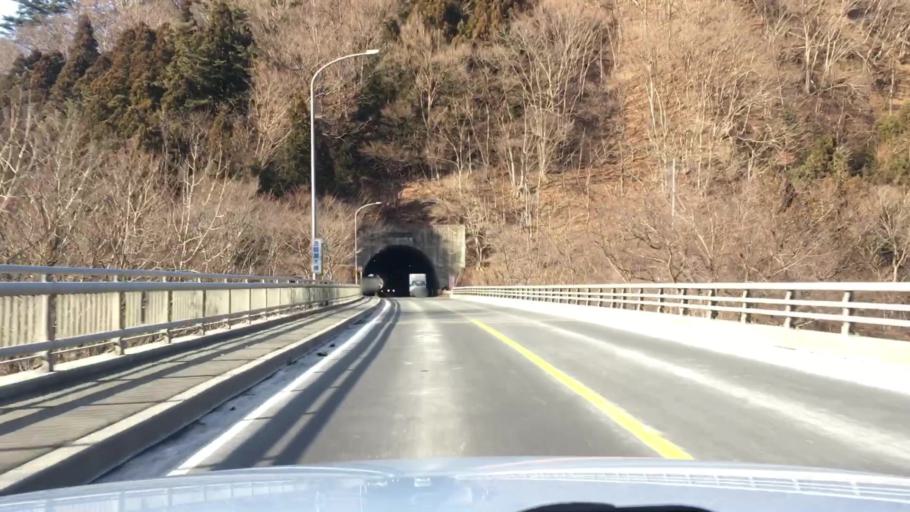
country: JP
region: Iwate
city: Tono
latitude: 39.6278
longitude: 141.6085
